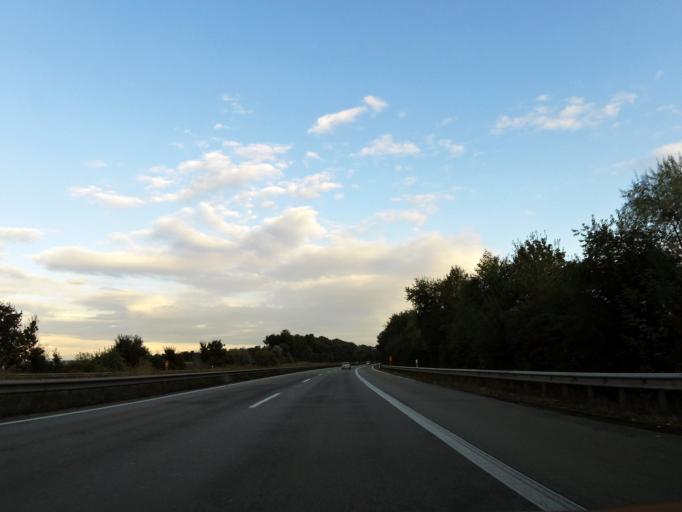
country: DE
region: Rheinland-Pfalz
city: Gau-Bickelheim
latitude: 49.8294
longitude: 8.0357
